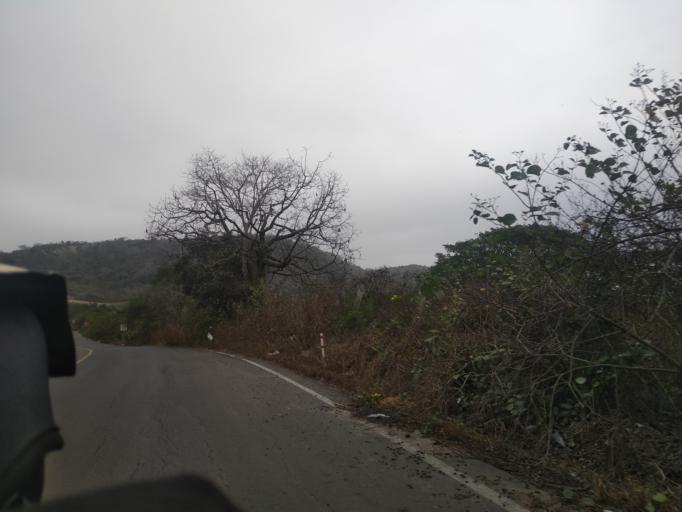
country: EC
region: Manabi
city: Montecristi
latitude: -1.0860
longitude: -80.6856
